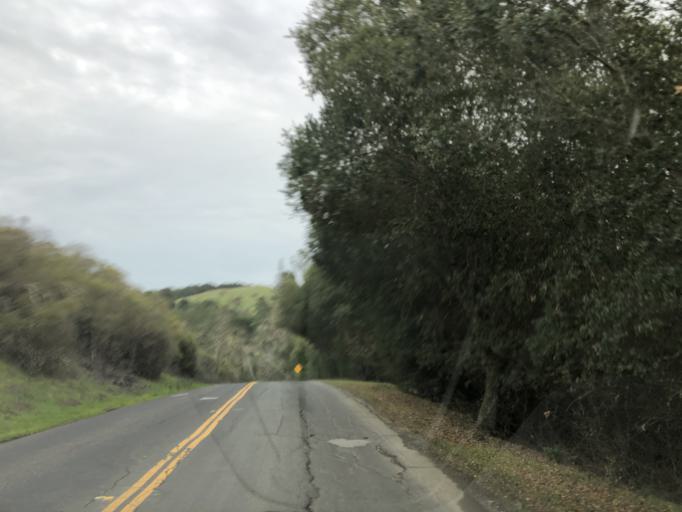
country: US
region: California
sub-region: Contra Costa County
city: Moraga
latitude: 37.8223
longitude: -122.1369
